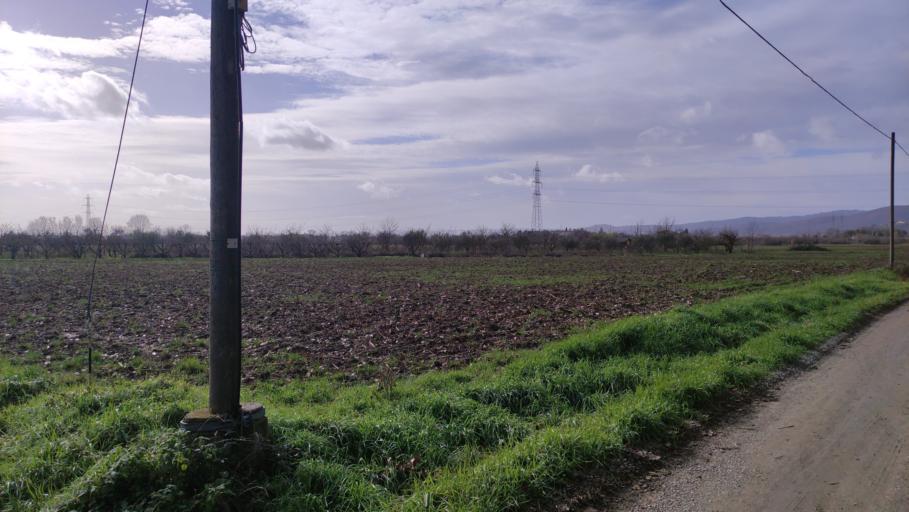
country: IT
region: Tuscany
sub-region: Province of Arezzo
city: Battifolle-Ruscello-Poggiola
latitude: 43.4298
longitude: 11.8075
